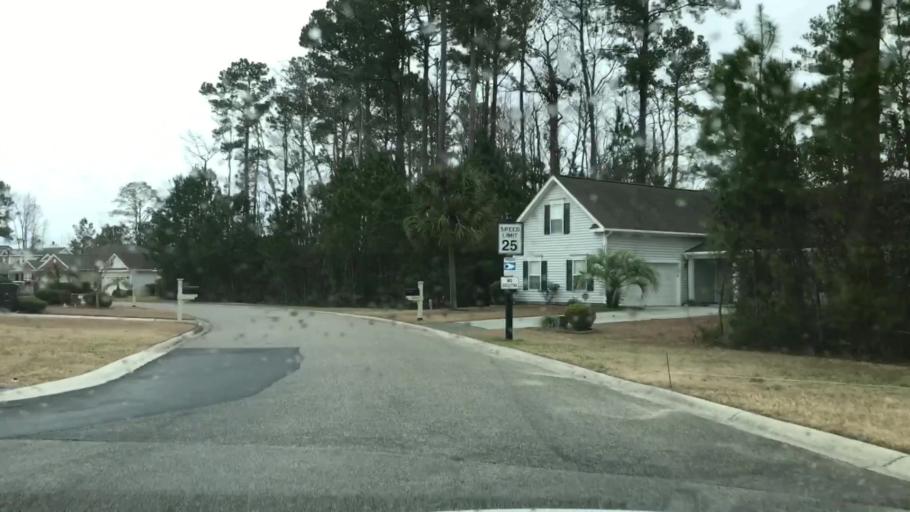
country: US
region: South Carolina
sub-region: Horry County
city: Red Hill
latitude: 33.7761
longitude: -79.0076
